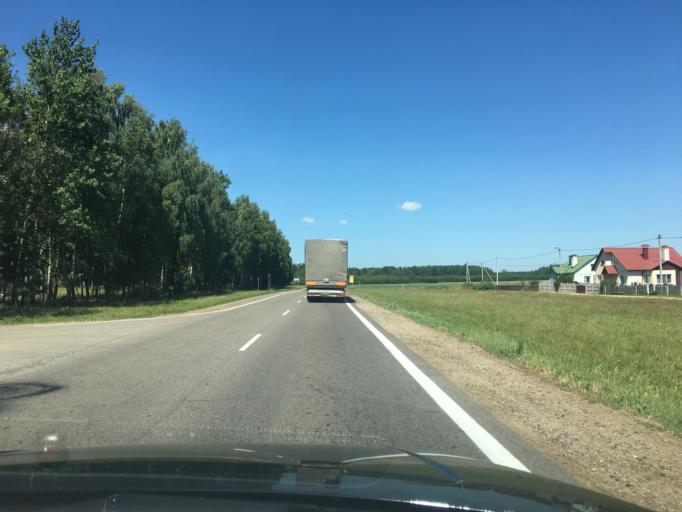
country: BY
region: Grodnenskaya
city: Iwye
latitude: 54.0378
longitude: 25.9200
